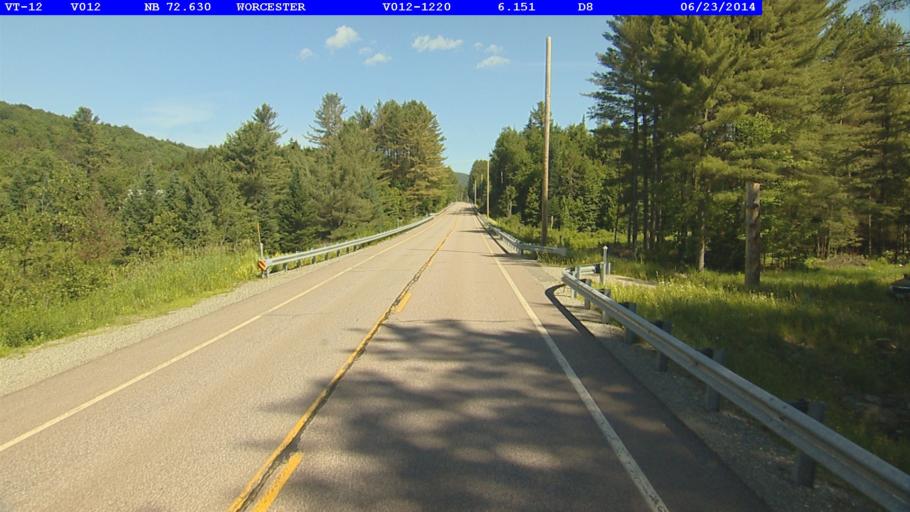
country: US
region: Vermont
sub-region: Lamoille County
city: Morrisville
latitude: 44.4302
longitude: -72.5333
